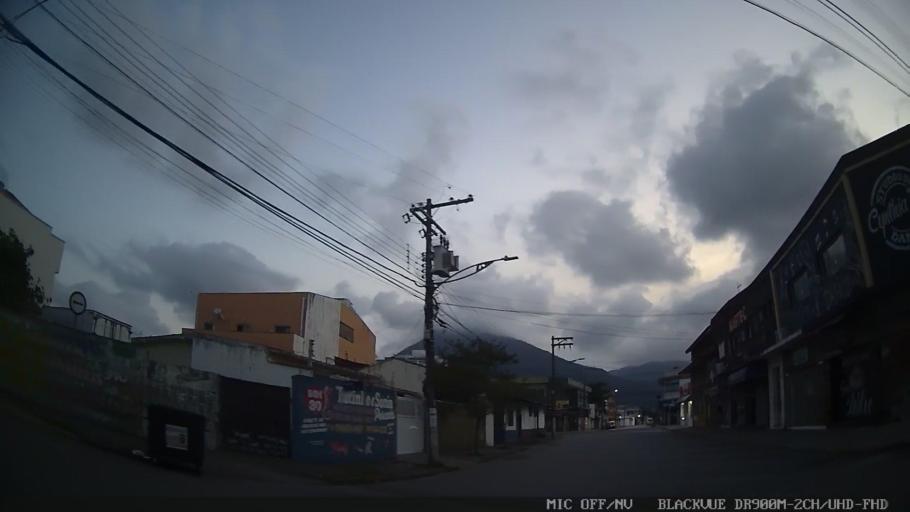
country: BR
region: Sao Paulo
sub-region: Peruibe
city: Peruibe
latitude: -24.3214
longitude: -46.9983
